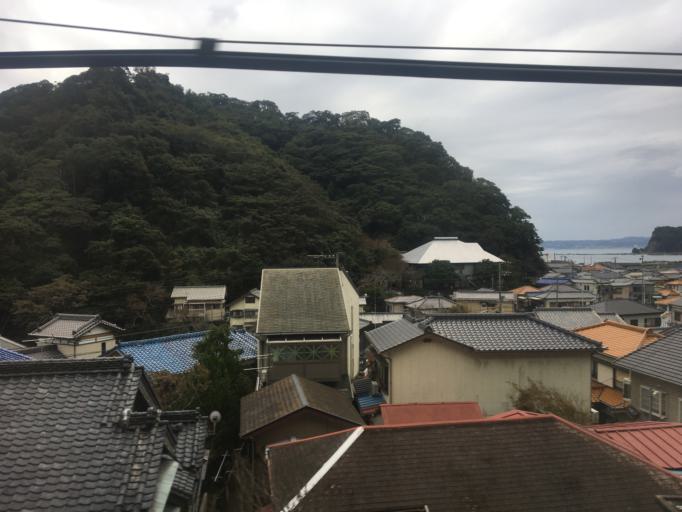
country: JP
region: Chiba
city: Kawaguchi
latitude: 35.1229
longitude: 140.2014
